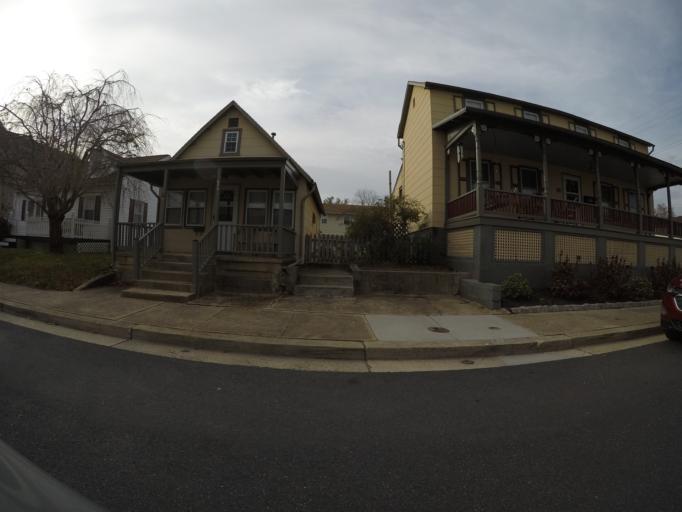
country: US
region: Maryland
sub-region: Harford County
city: Havre de Grace
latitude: 39.5443
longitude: -76.0880
